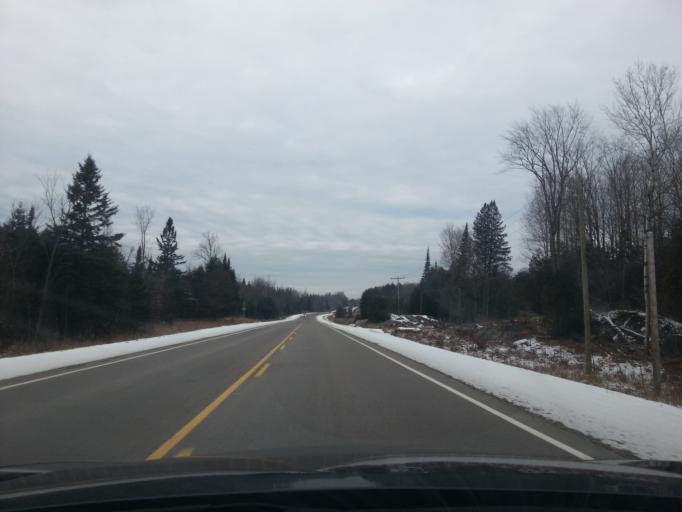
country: CA
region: Ontario
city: Skatepark
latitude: 44.7552
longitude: -76.8662
